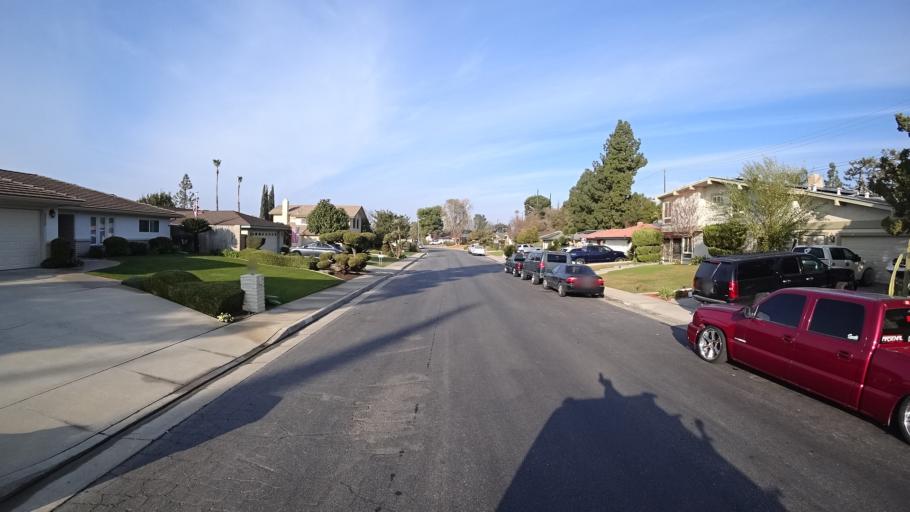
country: US
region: California
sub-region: Kern County
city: Oildale
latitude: 35.4110
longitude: -118.9567
